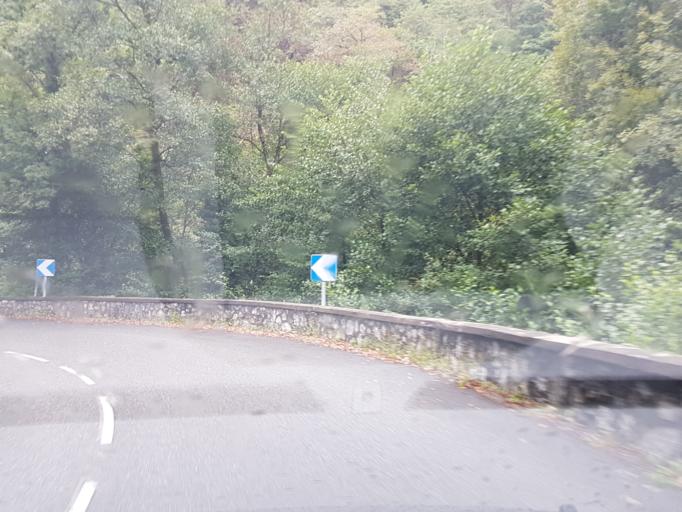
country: FR
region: Midi-Pyrenees
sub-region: Departement de l'Ariege
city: Saint-Girons
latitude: 42.9155
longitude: 1.2648
